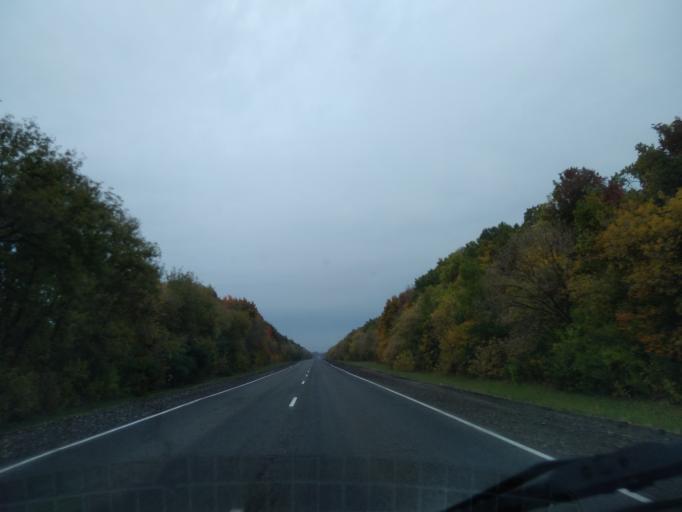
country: RU
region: Lipetsk
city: Zadonsk
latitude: 52.4640
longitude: 38.7732
